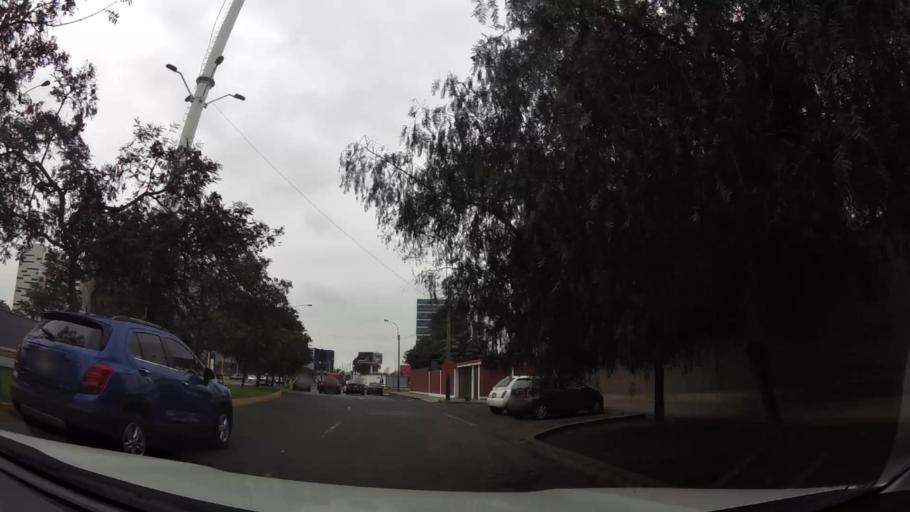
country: PE
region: Lima
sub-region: Lima
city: La Molina
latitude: -12.0990
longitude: -76.9684
